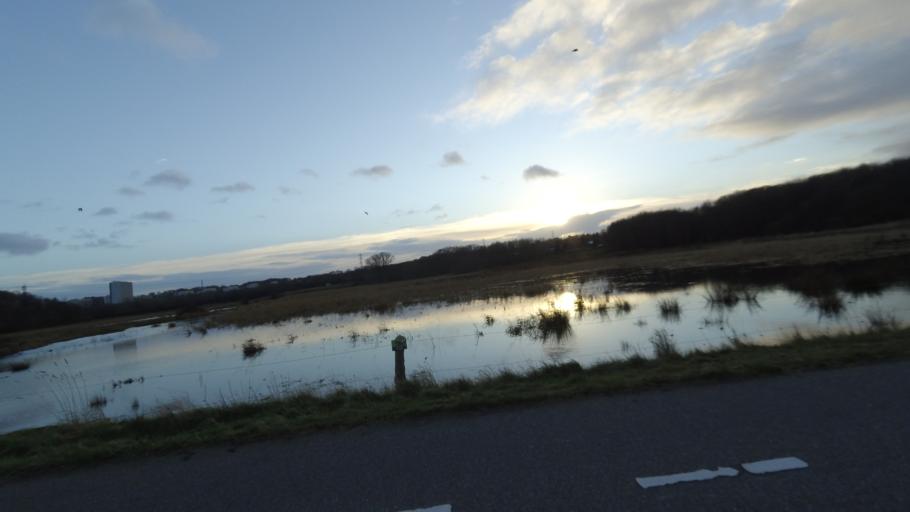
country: DK
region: Central Jutland
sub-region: Arhus Kommune
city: Stavtrup
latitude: 56.1339
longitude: 10.1338
